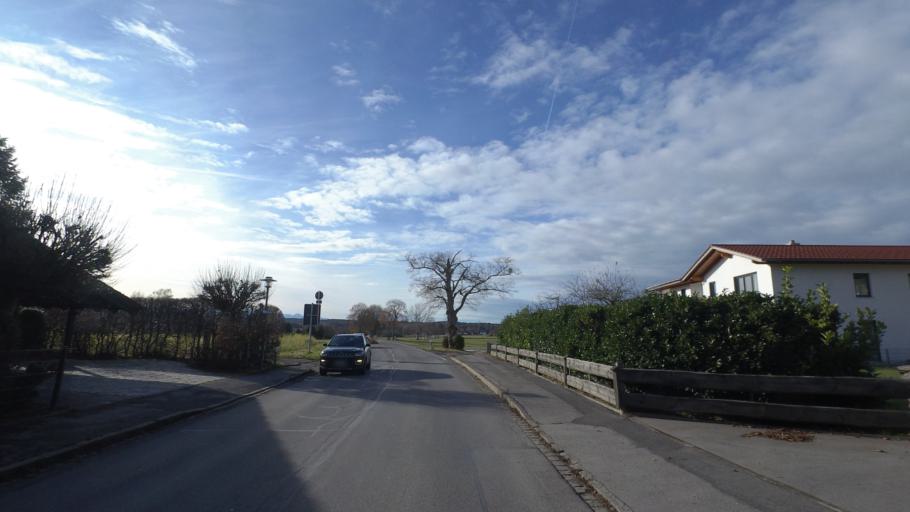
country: DE
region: Bavaria
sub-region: Upper Bavaria
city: Seeon-Seebruck
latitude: 47.9359
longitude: 12.4707
